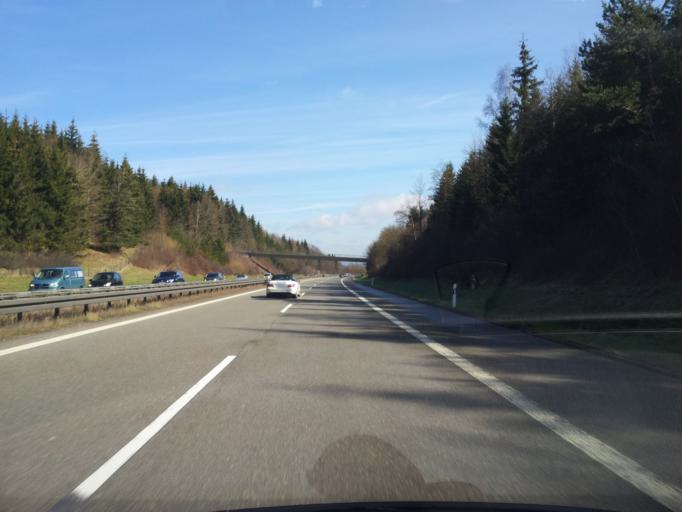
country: DE
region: Baden-Wuerttemberg
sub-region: Freiburg Region
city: Villingendorf
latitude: 48.1835
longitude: 8.5784
